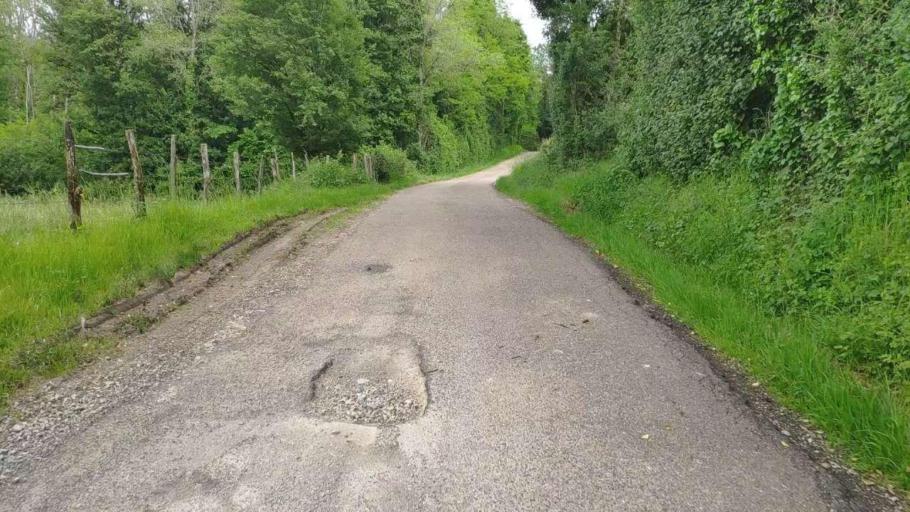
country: FR
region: Franche-Comte
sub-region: Departement du Jura
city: Montmorot
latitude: 46.7478
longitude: 5.5297
